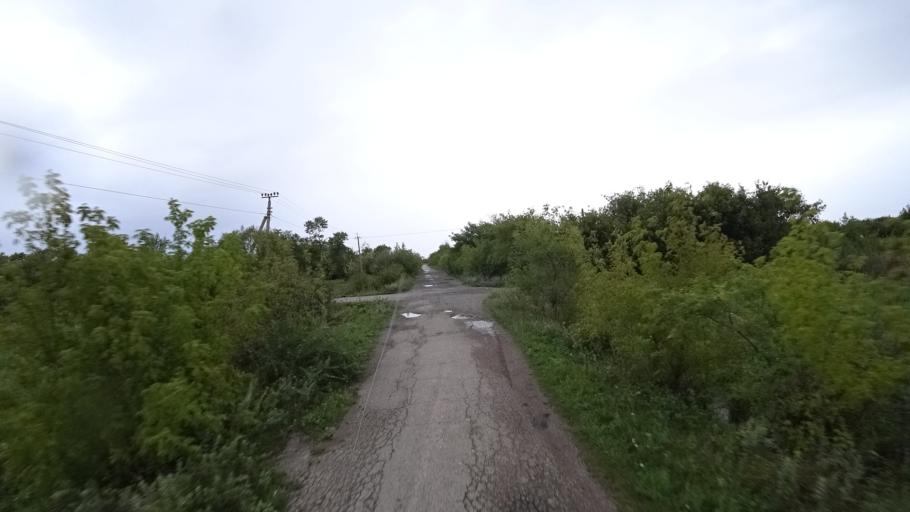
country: RU
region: Primorskiy
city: Chernigovka
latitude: 44.4021
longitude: 132.5316
